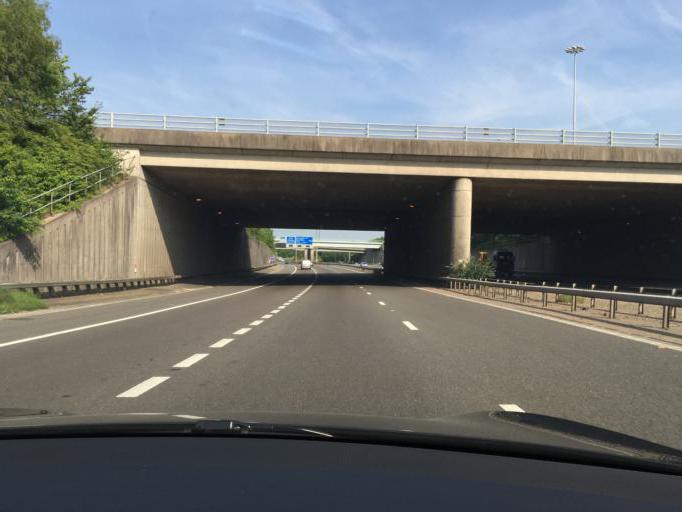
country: GB
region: England
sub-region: Manchester
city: Failsworth
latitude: 53.5195
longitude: -2.1427
